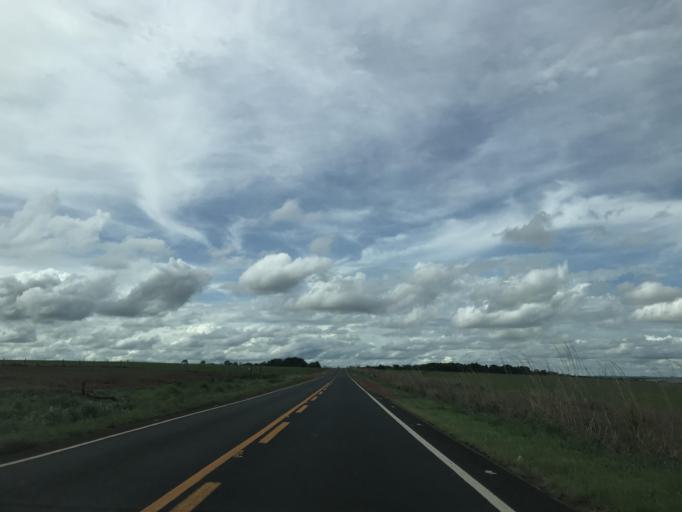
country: BR
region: Goias
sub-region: Piracanjuba
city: Piracanjuba
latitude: -17.4494
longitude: -48.7785
